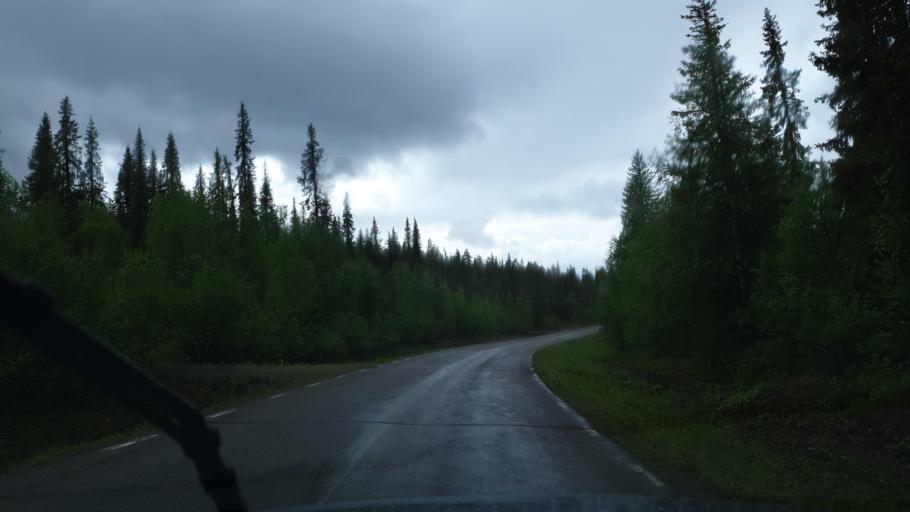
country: SE
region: Norrbotten
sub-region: Gallivare Kommun
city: Malmberget
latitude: 67.8905
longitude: 21.0422
